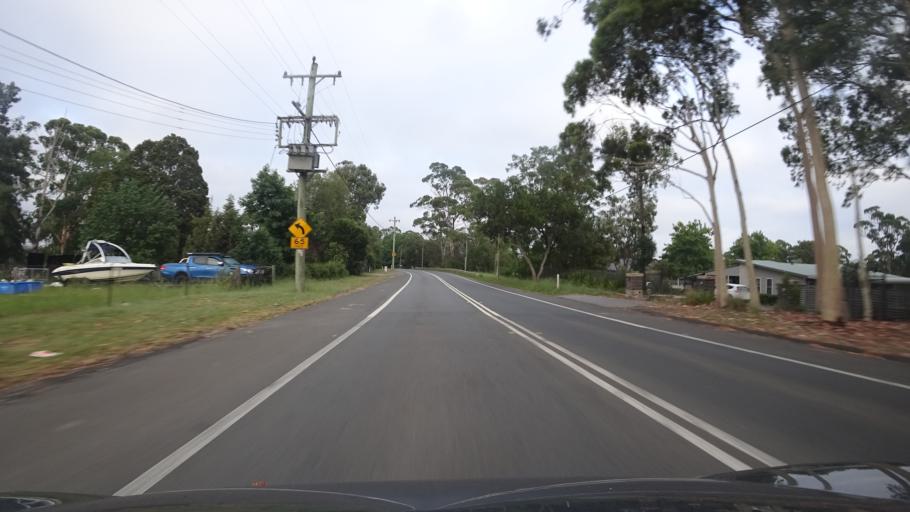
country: AU
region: New South Wales
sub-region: Blacktown
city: Rouse Hill
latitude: -33.6562
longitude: 150.9386
